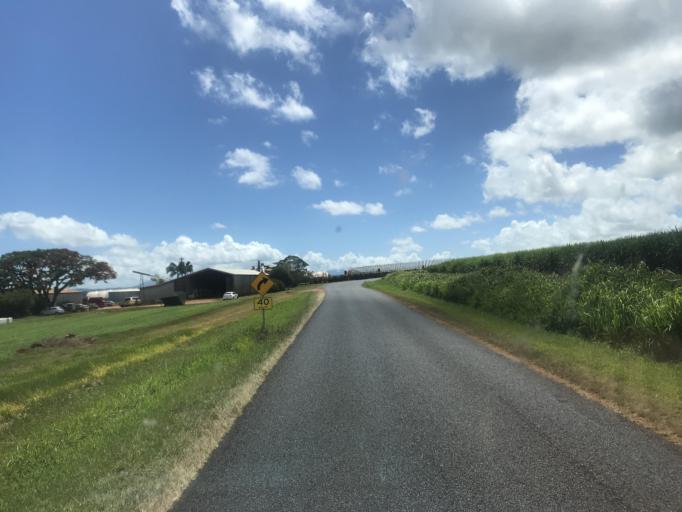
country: AU
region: Queensland
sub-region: Tablelands
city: Tolga
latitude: -17.2367
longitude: 145.5131
